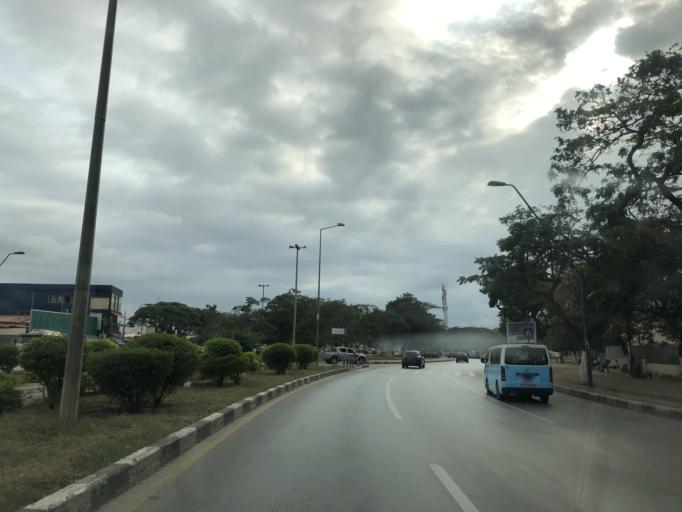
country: AO
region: Luanda
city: Luanda
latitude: -8.8378
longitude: 13.2363
